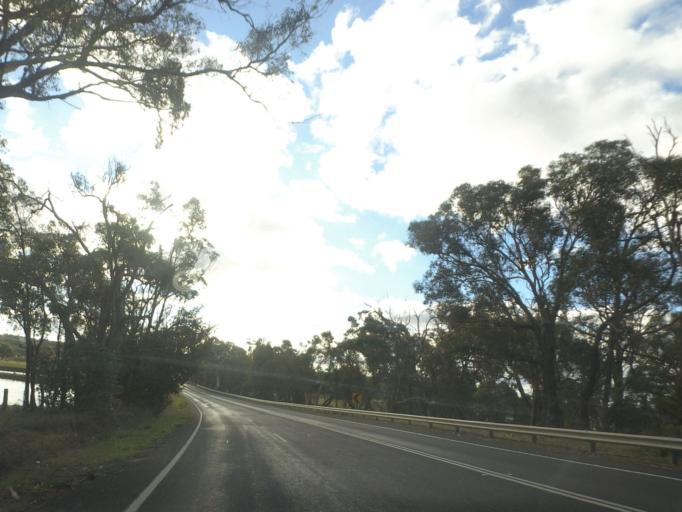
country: AU
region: Victoria
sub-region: Mount Alexander
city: Castlemaine
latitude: -37.1247
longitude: 144.3443
